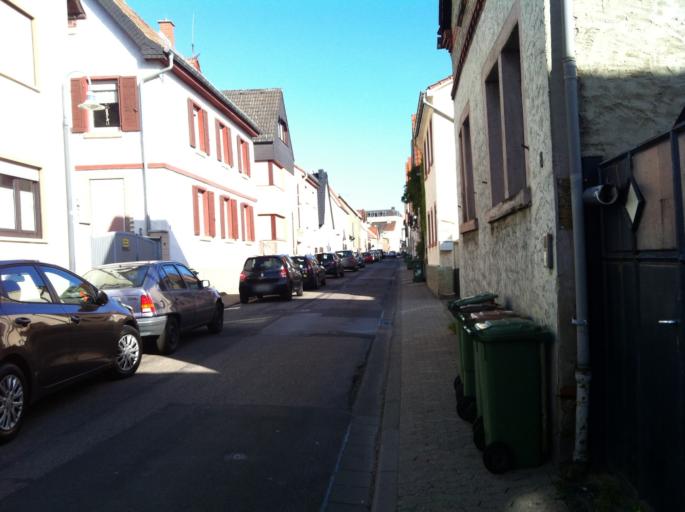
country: DE
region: Rheinland-Pfalz
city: Budenheim
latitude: 50.0013
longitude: 8.2119
